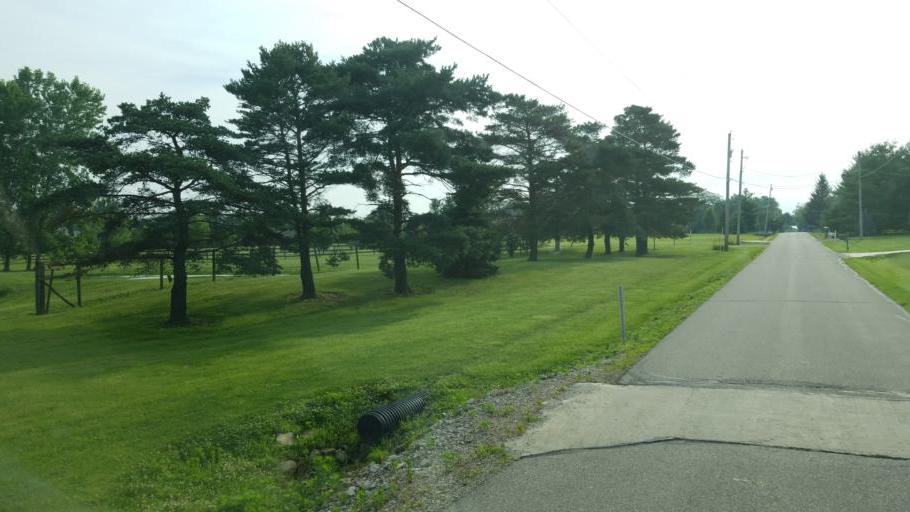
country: US
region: Ohio
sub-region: Union County
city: New California
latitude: 40.2016
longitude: -83.1626
